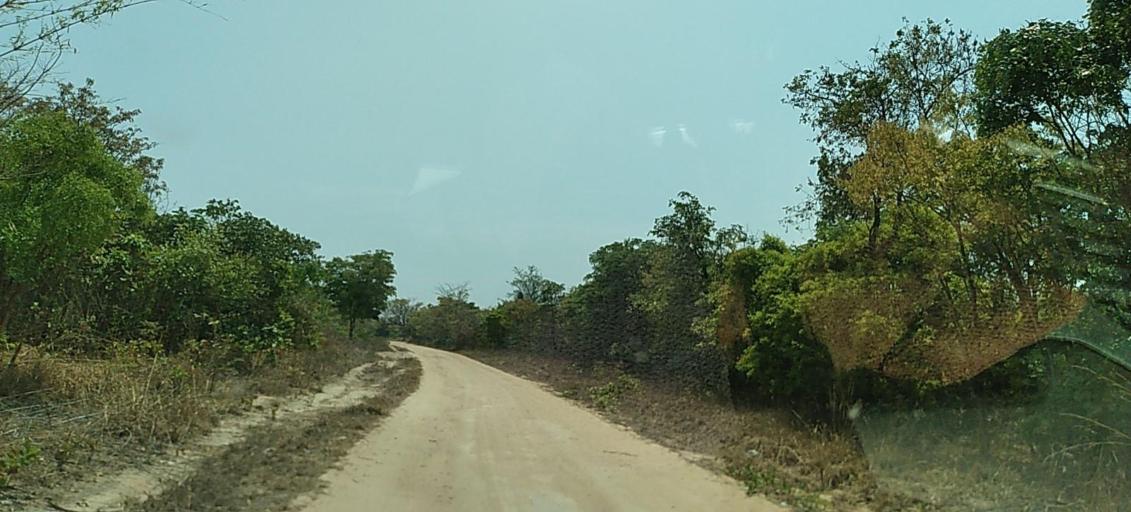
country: ZM
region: Copperbelt
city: Kalulushi
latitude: -12.9403
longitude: 28.1589
